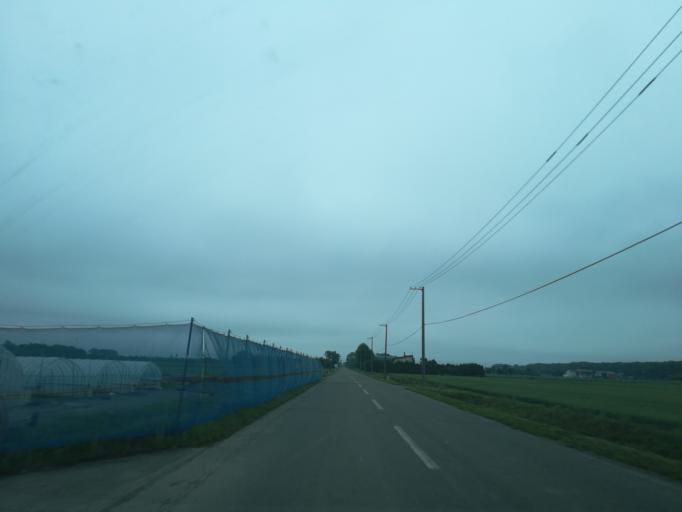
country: JP
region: Hokkaido
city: Ebetsu
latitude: 43.0641
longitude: 141.6303
